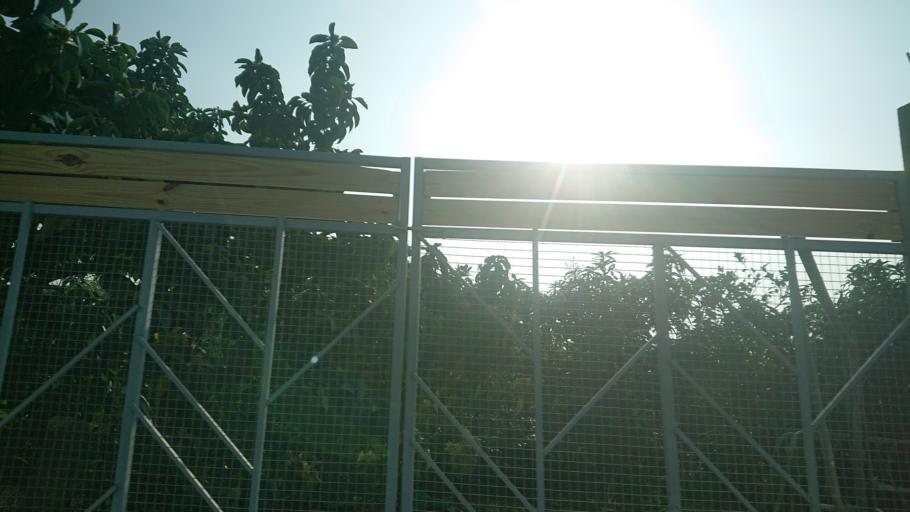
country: TW
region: Taiwan
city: Xinying
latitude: 23.1755
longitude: 120.2605
